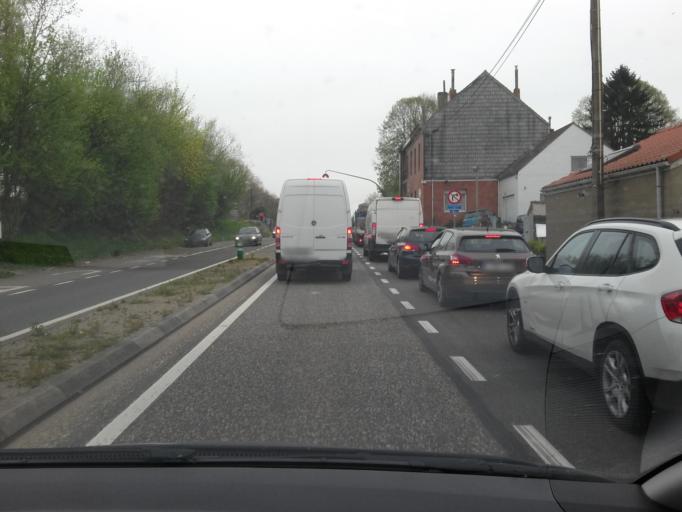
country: BE
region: Wallonia
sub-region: Province du Brabant Wallon
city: Waterloo
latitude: 50.6813
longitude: 4.4115
